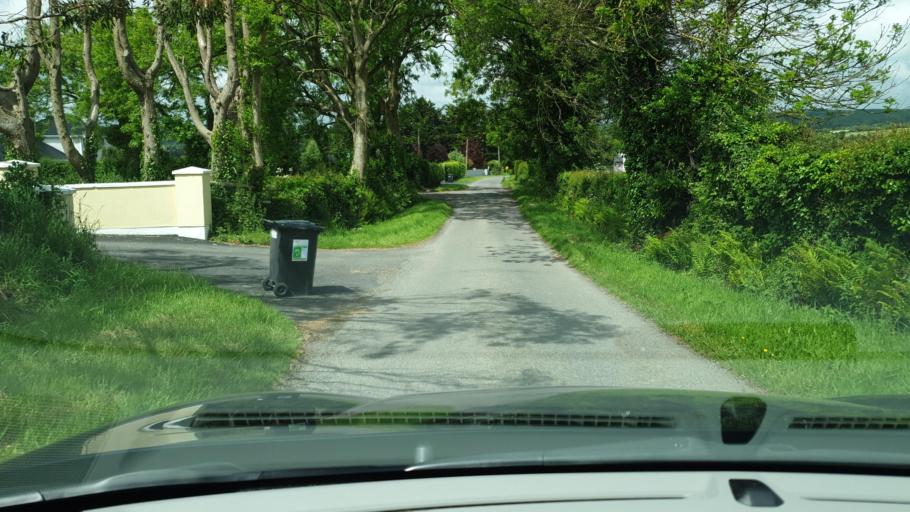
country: IE
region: Leinster
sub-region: An Mhi
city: Slane
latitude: 53.7398
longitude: -6.5649
